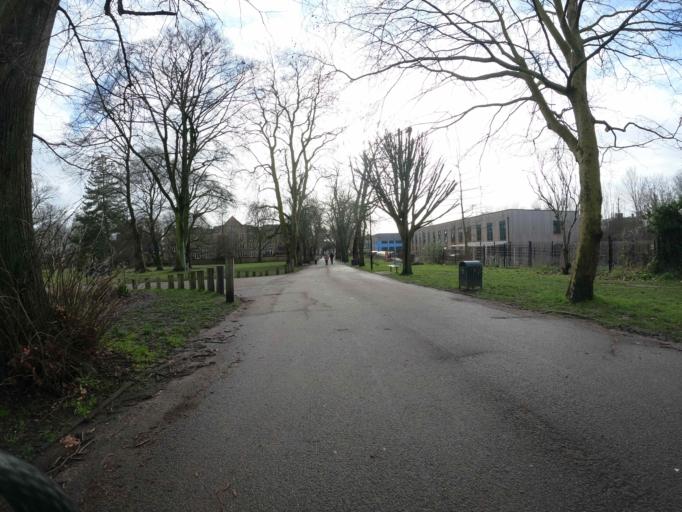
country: GB
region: England
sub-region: Greater London
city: Acton
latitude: 51.5079
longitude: -0.2621
